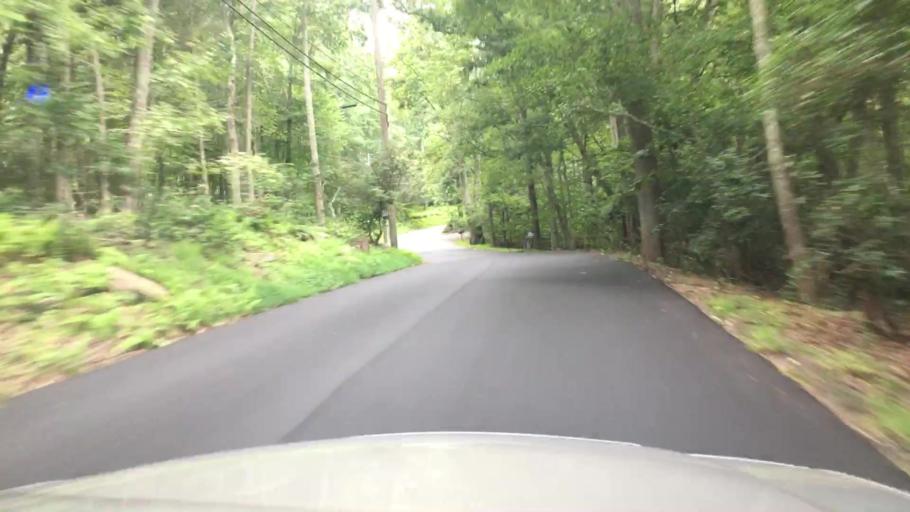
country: US
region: Connecticut
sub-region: Middlesex County
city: Essex Village
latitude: 41.3844
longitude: -72.3975
